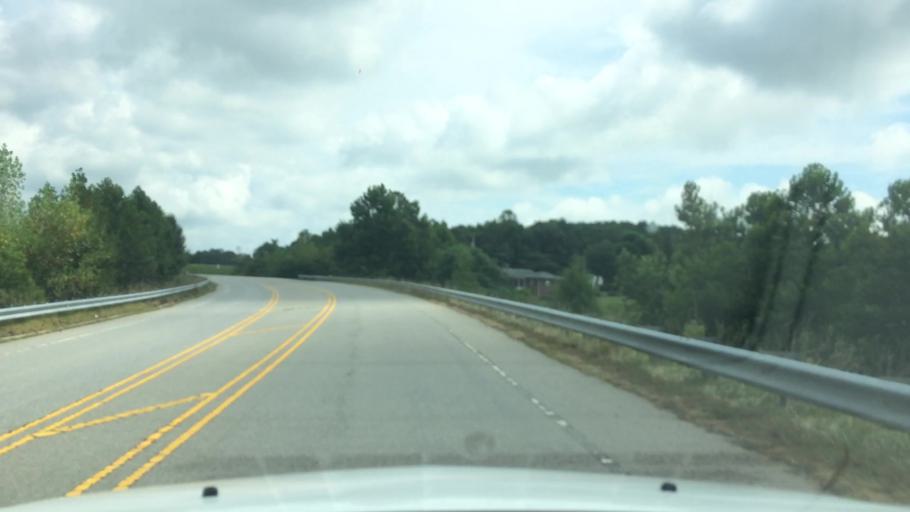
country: US
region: North Carolina
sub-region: Yadkin County
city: Jonesville
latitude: 36.1264
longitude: -80.8434
